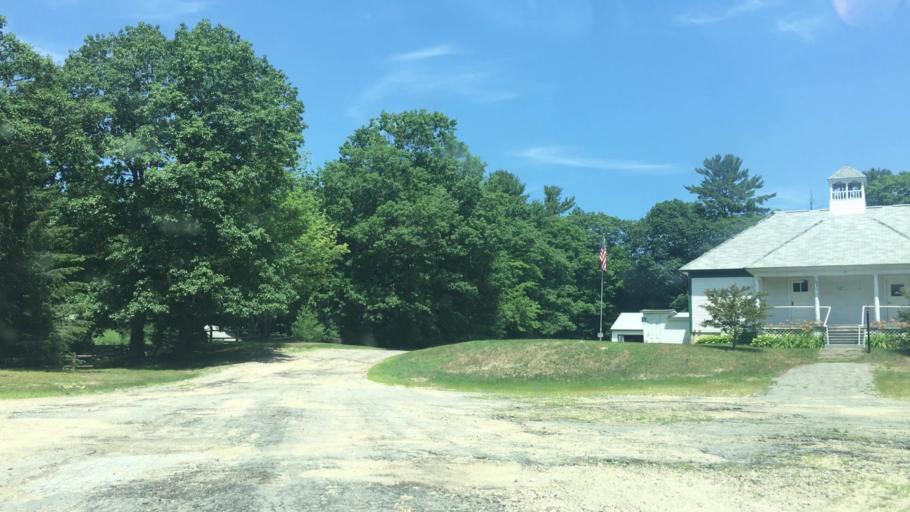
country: US
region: Maine
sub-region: Androscoggin County
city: Livermore
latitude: 44.3852
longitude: -70.2516
